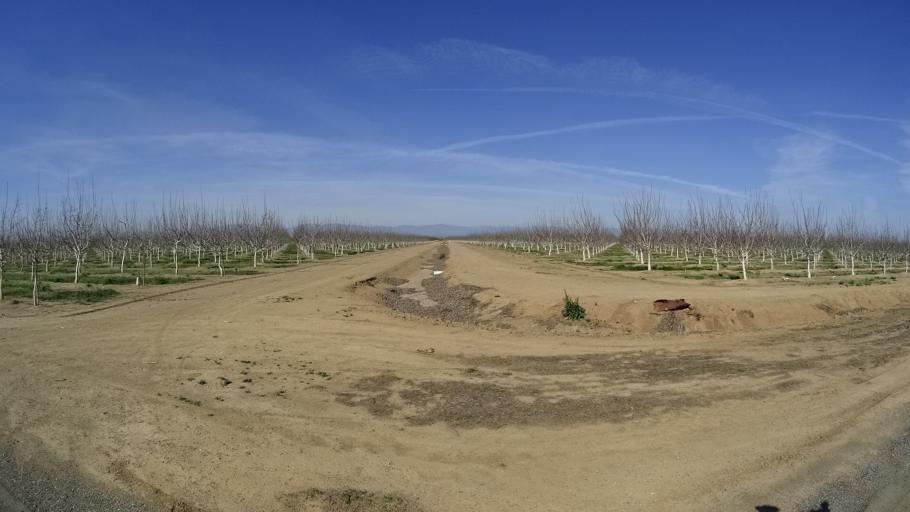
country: US
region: California
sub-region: Glenn County
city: Willows
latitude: 39.6177
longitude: -122.2129
